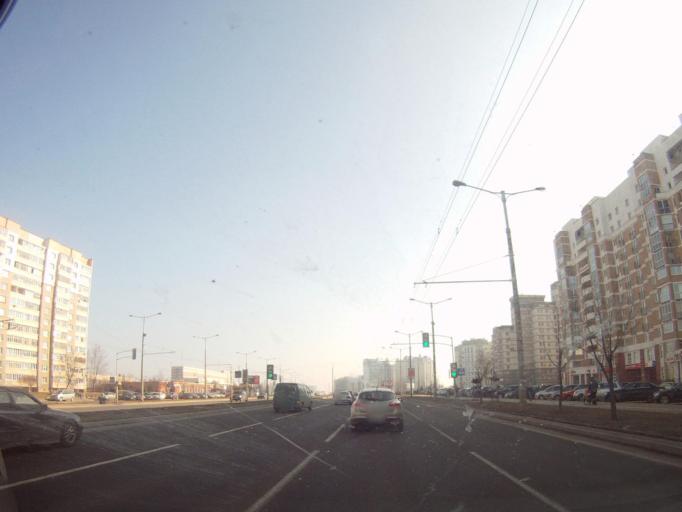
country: BY
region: Minsk
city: Novoye Medvezhino
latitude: 53.9062
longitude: 27.4492
